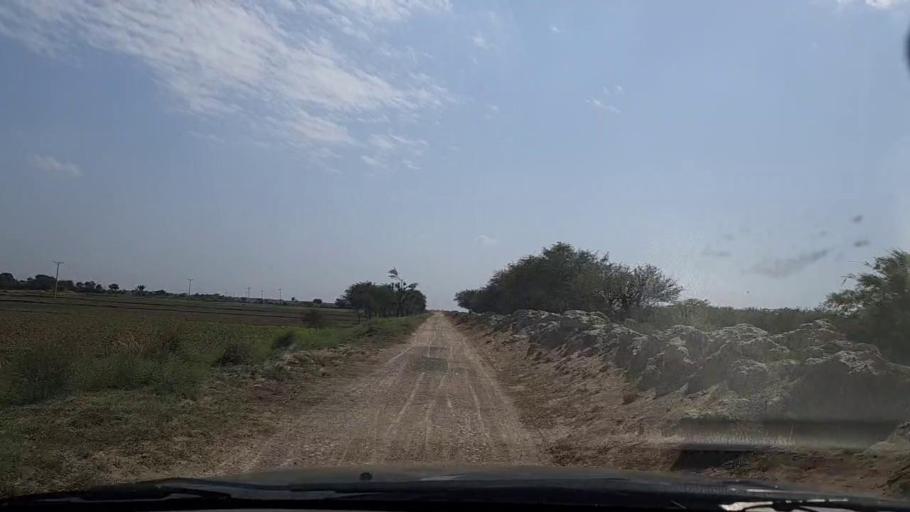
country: PK
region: Sindh
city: Mirpur Batoro
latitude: 24.5842
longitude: 68.1963
